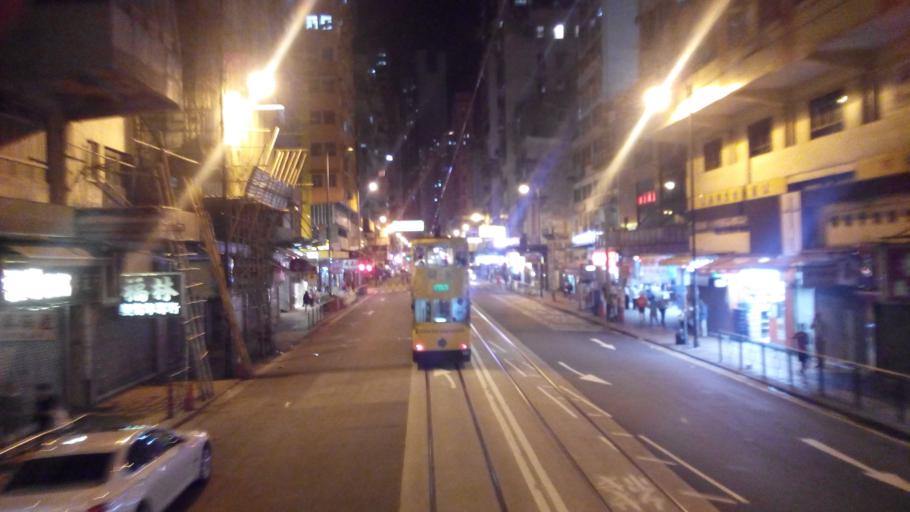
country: HK
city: Hong Kong
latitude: 22.2878
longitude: 114.1450
